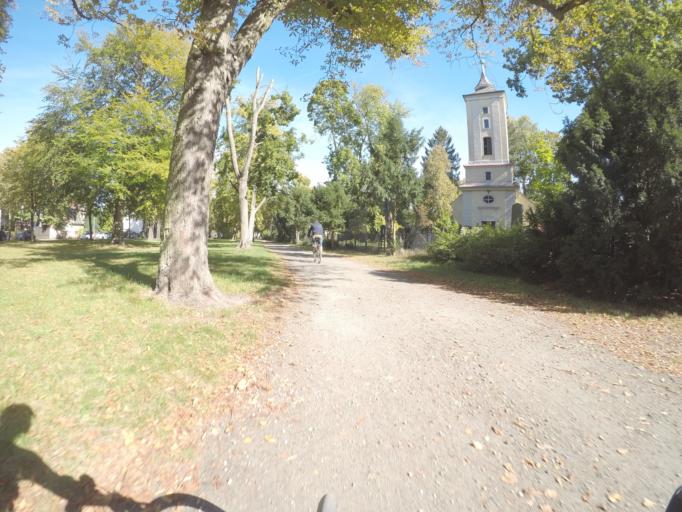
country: DE
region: Berlin
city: Konradshohe
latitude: 52.6077
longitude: 13.2123
